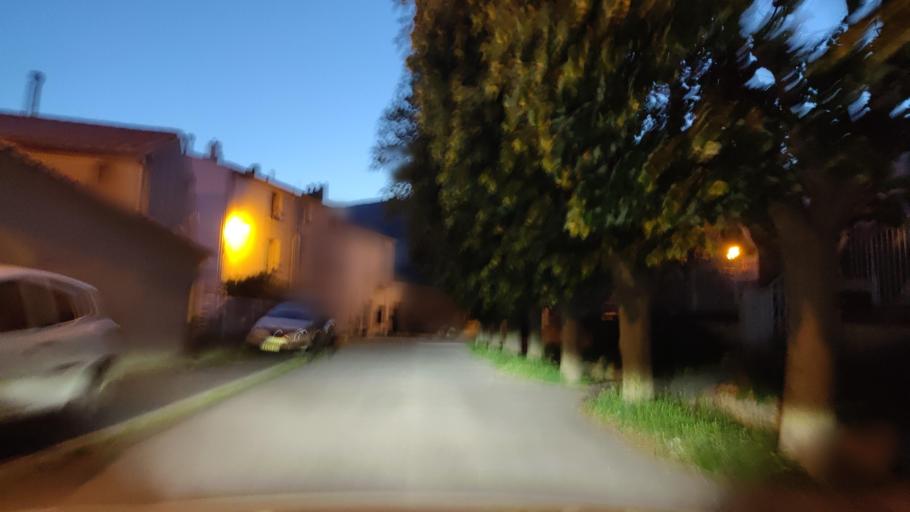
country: FR
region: Languedoc-Roussillon
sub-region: Departement des Pyrenees-Orientales
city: Estagel
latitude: 42.8867
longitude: 2.7221
